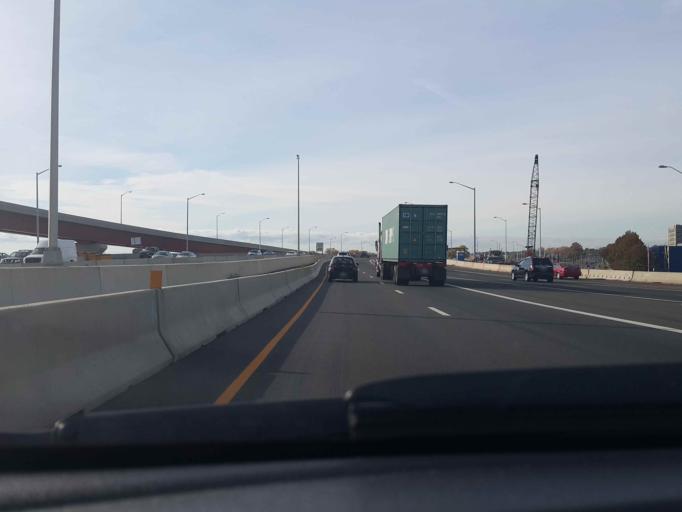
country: US
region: Connecticut
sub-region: New Haven County
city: New Haven
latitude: 41.2981
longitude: -72.9163
